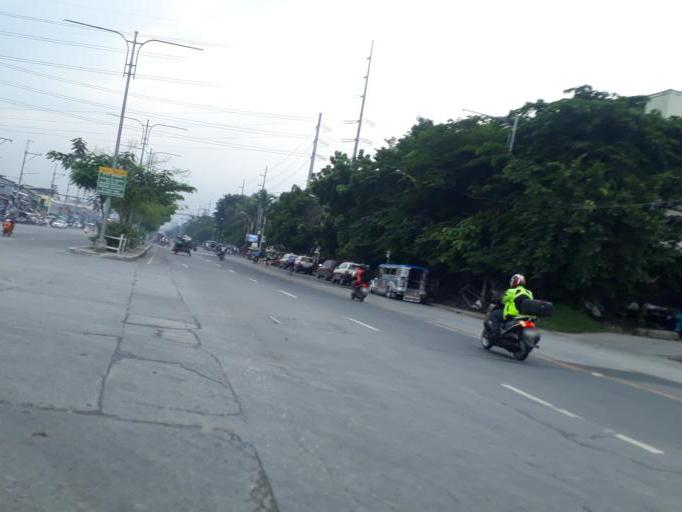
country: PH
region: Metro Manila
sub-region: Caloocan City
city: Niugan
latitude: 14.6458
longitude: 120.9516
